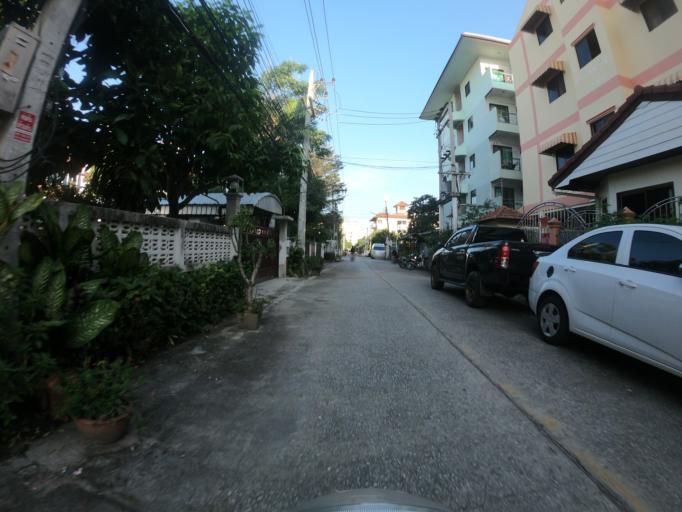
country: TH
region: Chiang Mai
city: Chiang Mai
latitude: 18.8040
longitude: 98.9901
